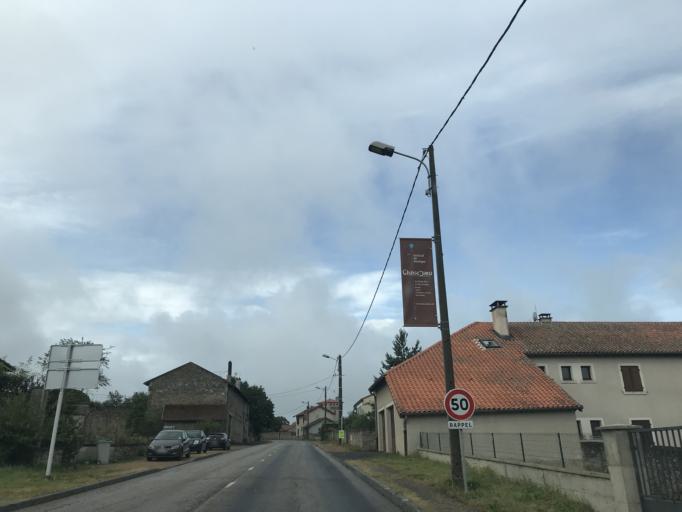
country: FR
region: Auvergne
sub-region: Departement de la Haute-Loire
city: Fontannes
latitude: 45.3238
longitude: 3.6983
